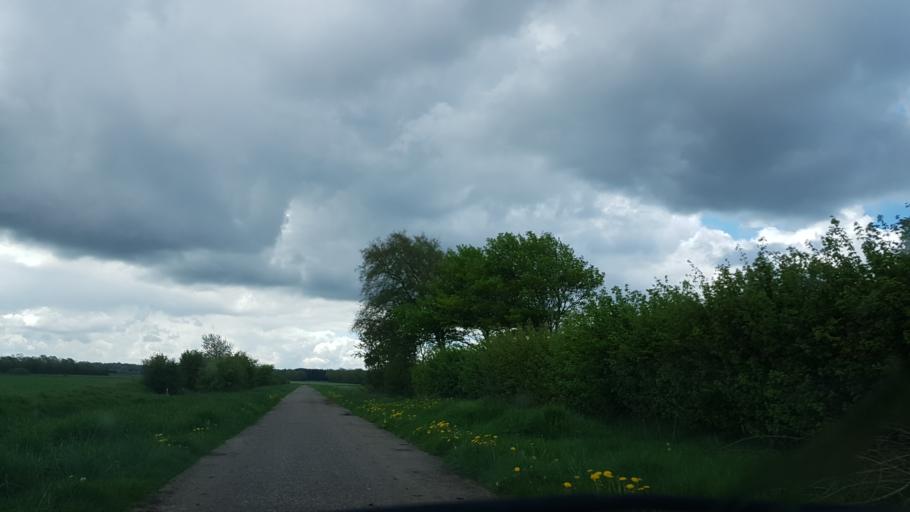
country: DK
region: South Denmark
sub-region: Haderslev Kommune
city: Vojens
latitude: 55.2425
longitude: 9.1945
